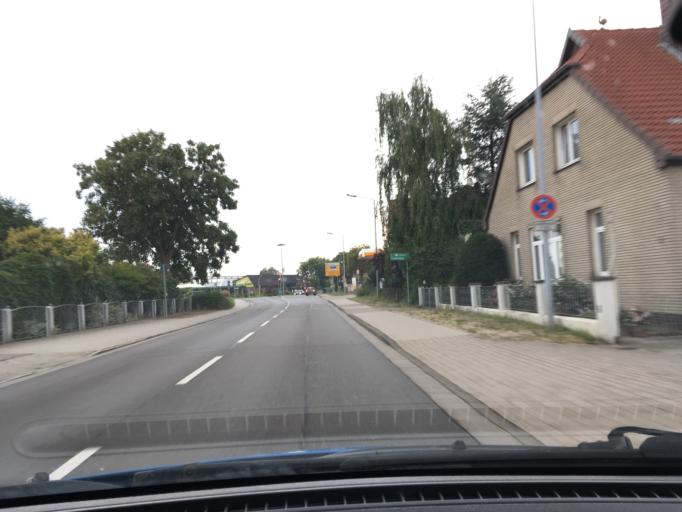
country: DE
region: Lower Saxony
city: Celle
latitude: 52.6362
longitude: 10.1076
